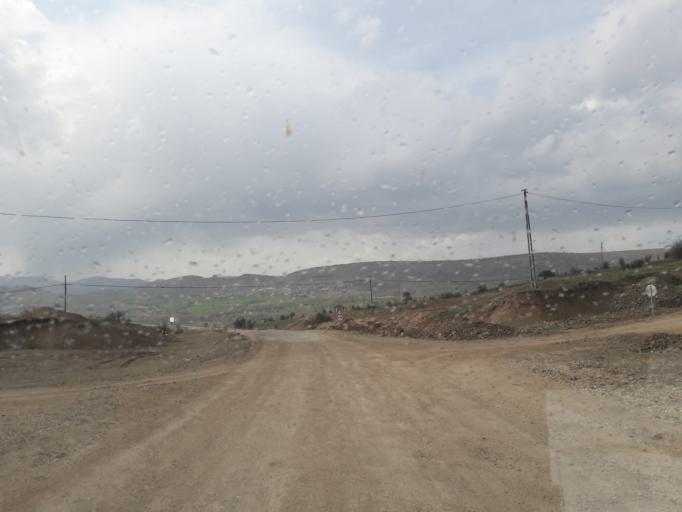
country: TR
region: Giresun
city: Alucra
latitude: 40.3199
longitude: 38.7738
